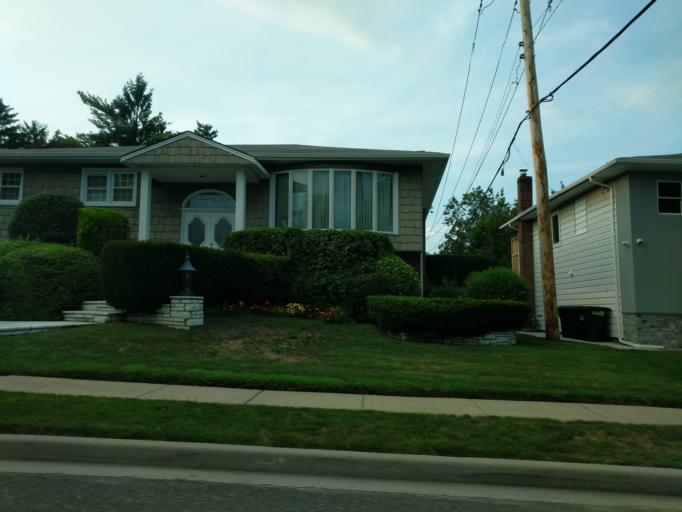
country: US
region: New York
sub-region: Nassau County
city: South Valley Stream
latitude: 40.6445
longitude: -73.7249
